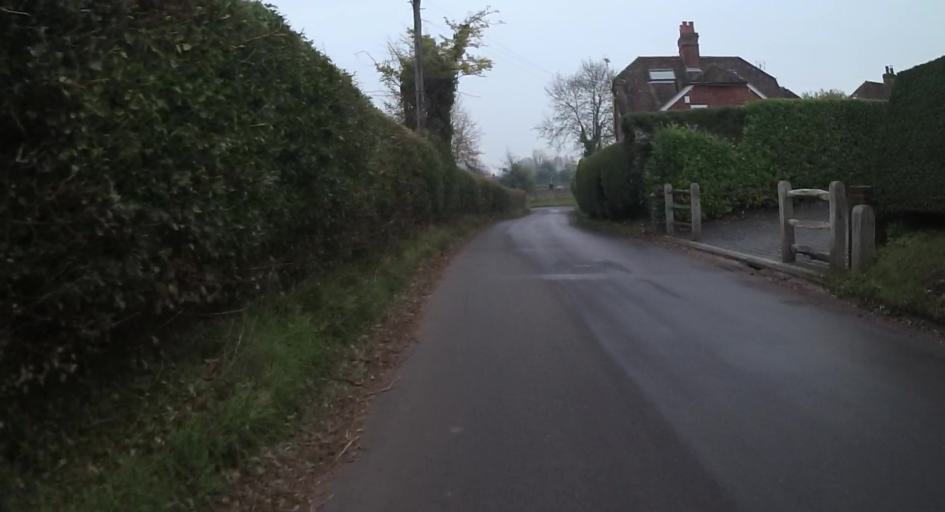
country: GB
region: England
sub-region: Hampshire
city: Long Sutton
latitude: 51.1913
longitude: -0.9090
